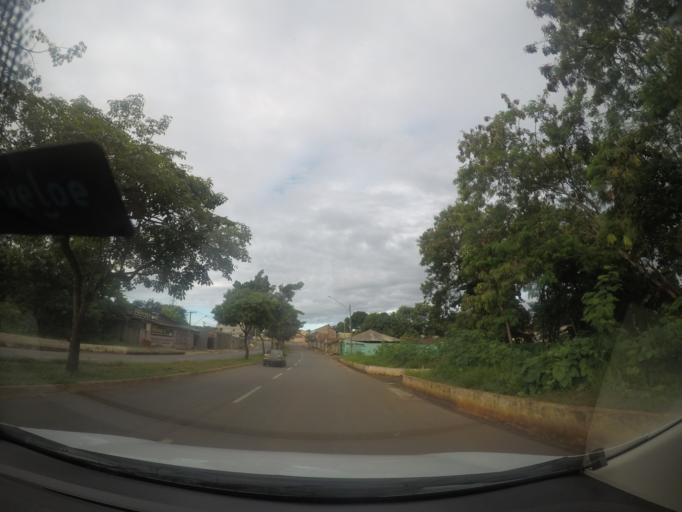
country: BR
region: Goias
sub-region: Goiania
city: Goiania
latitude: -16.6089
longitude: -49.3408
